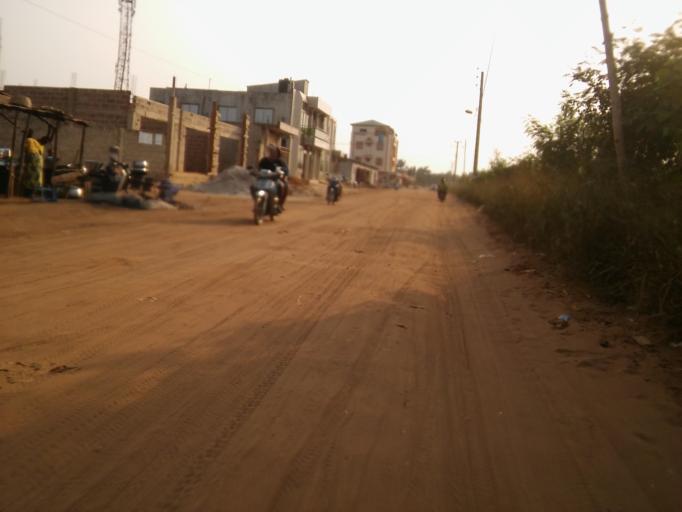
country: BJ
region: Atlantique
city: Abomey-Calavi
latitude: 6.4163
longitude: 2.3337
